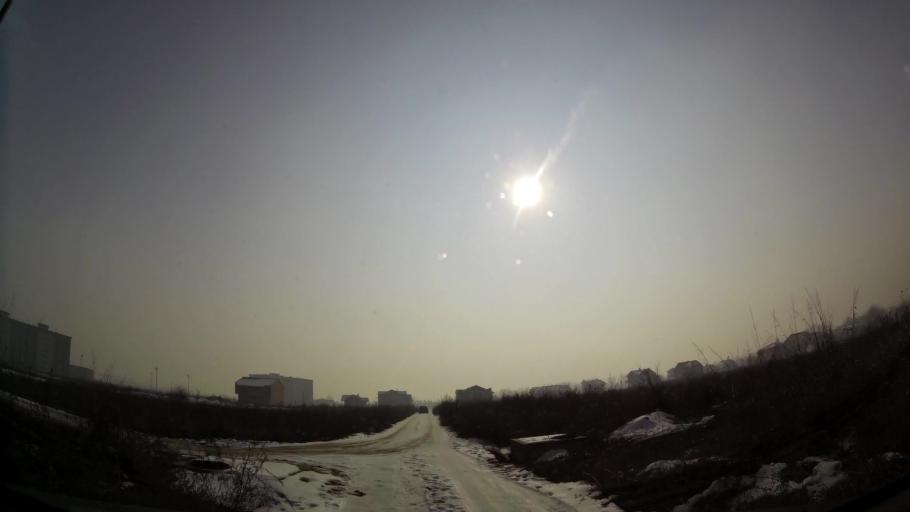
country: MK
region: Kisela Voda
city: Kisela Voda
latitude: 41.9948
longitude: 21.5171
